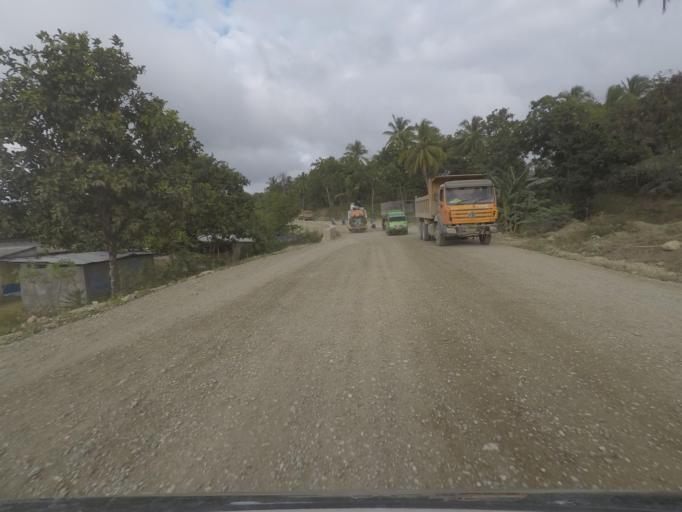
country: TL
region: Baucau
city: Baucau
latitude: -8.5136
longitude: 126.4409
